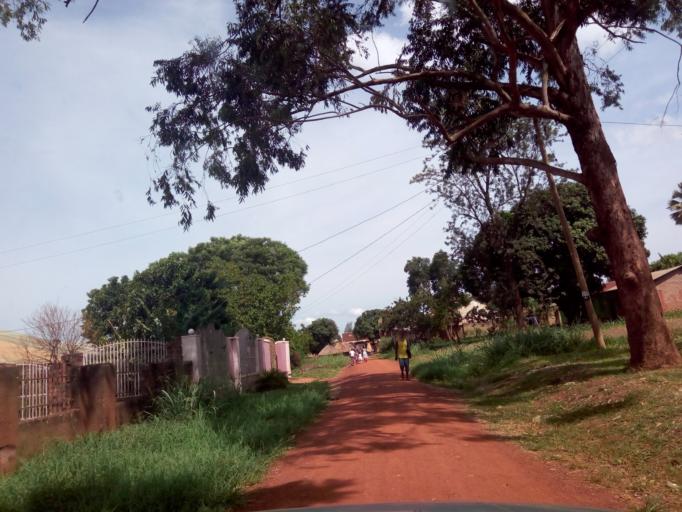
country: UG
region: Western Region
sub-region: Masindi District
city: Masindi
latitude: 1.6797
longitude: 31.7193
